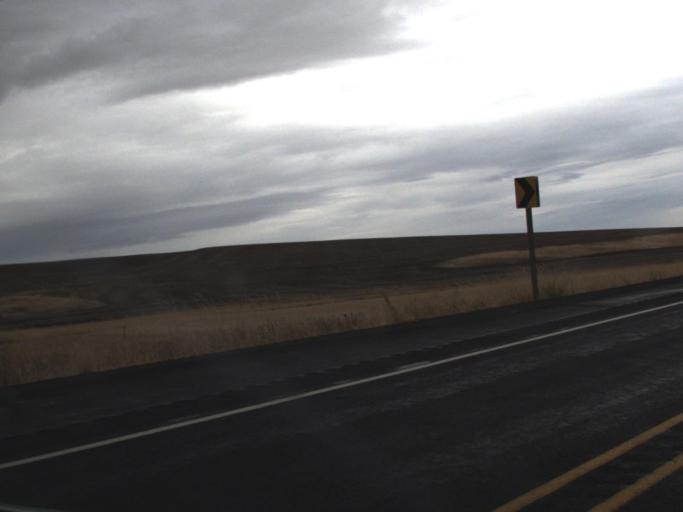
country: US
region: Washington
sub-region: Asotin County
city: Clarkston
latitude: 46.5586
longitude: -117.1049
